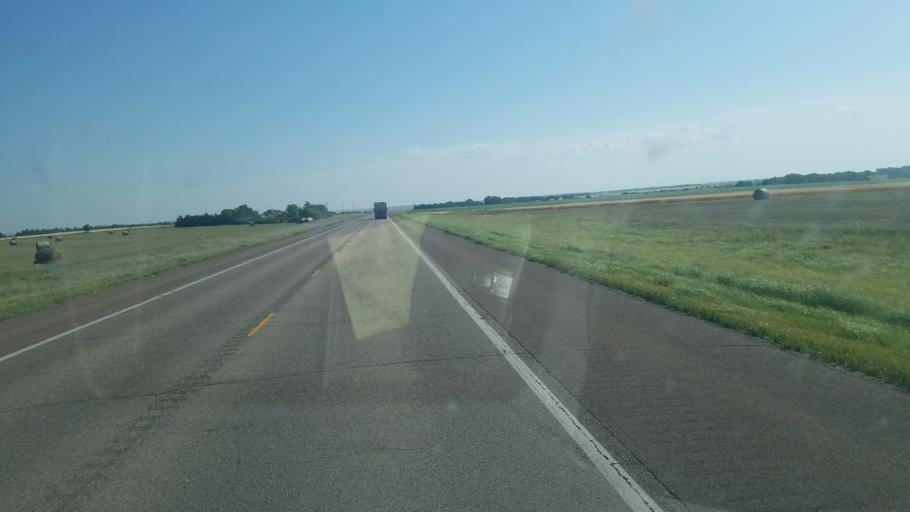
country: US
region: Kansas
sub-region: Barton County
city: Great Bend
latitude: 38.3935
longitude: -98.6747
